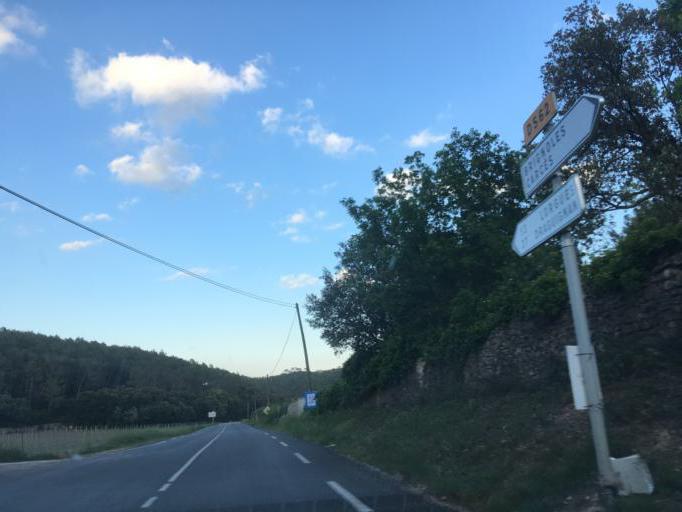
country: FR
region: Provence-Alpes-Cote d'Azur
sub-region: Departement du Var
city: Carces
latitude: 43.4854
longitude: 6.2162
